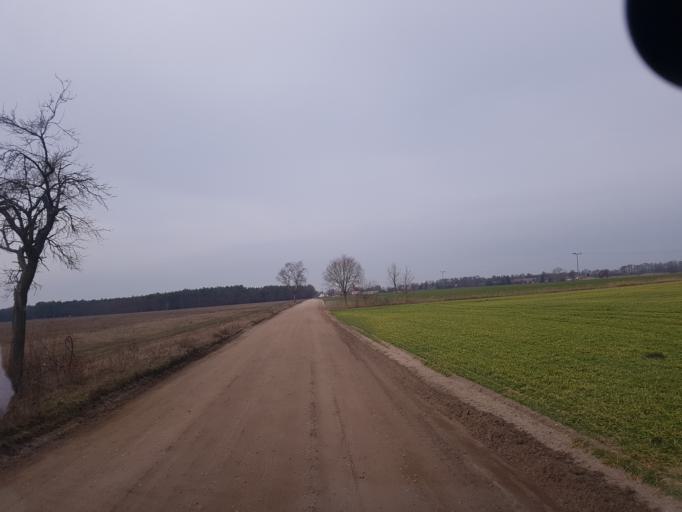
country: DE
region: Brandenburg
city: Sonnewalde
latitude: 51.6627
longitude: 13.6598
